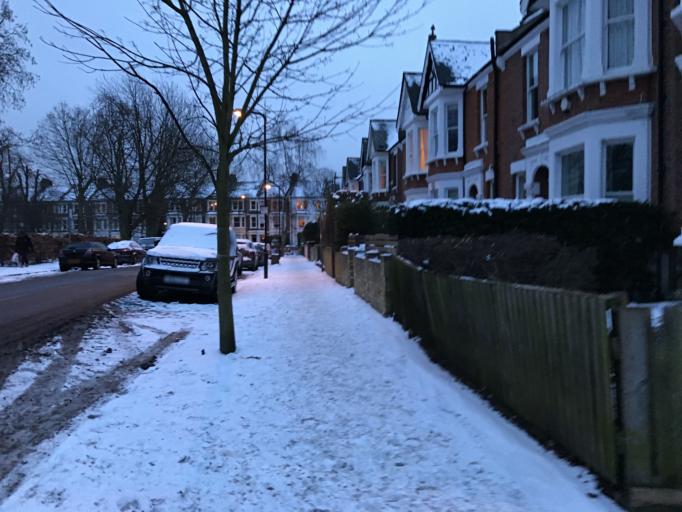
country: GB
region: England
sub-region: Greater London
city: Bayswater
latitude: 51.5342
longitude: -0.2119
